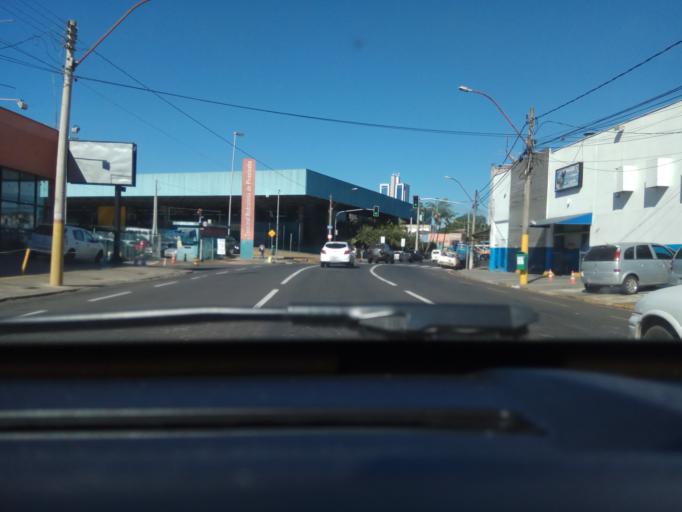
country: BR
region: Sao Paulo
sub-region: Piracicaba
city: Piracicaba
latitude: -22.7303
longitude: -47.6483
